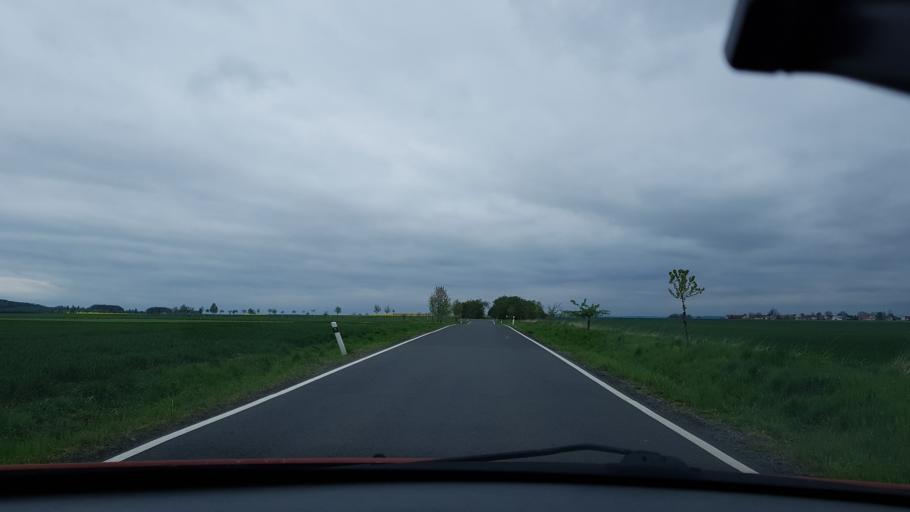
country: CZ
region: Olomoucky
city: Vidnava
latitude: 50.3758
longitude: 17.1749
